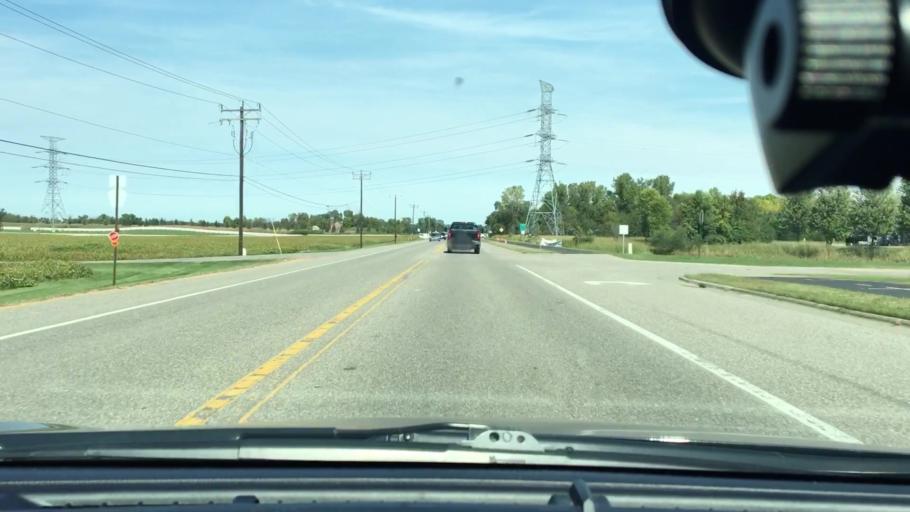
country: US
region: Minnesota
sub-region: Wright County
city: Hanover
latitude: 45.1267
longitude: -93.6357
